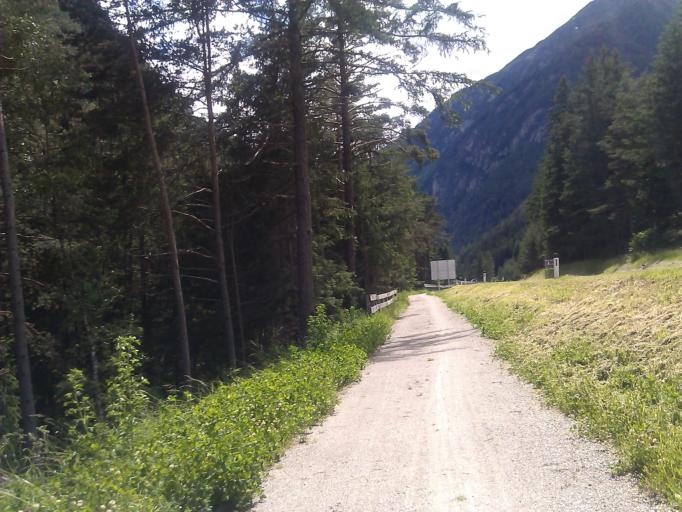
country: AT
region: Tyrol
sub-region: Politischer Bezirk Landeck
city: Pfunds
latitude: 46.9449
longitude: 10.5025
